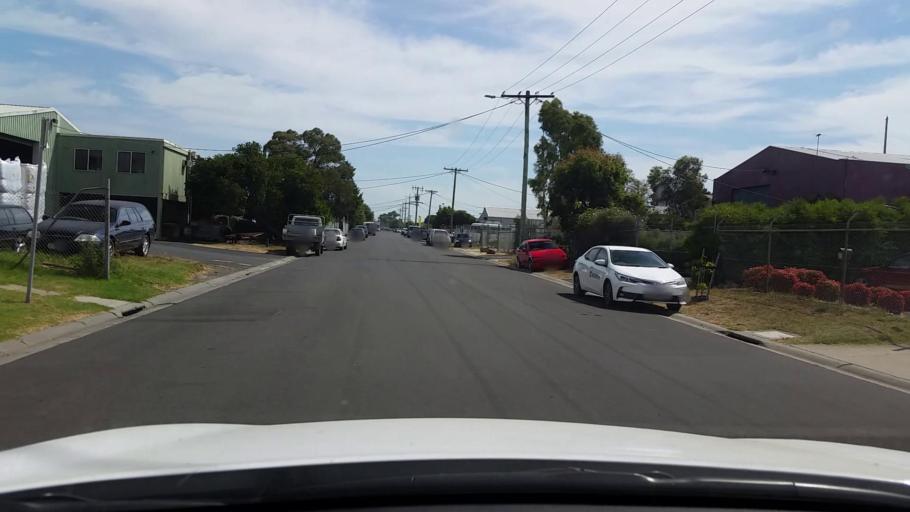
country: AU
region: Victoria
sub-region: Mornington Peninsula
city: Hastings
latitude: -38.3068
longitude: 145.1848
